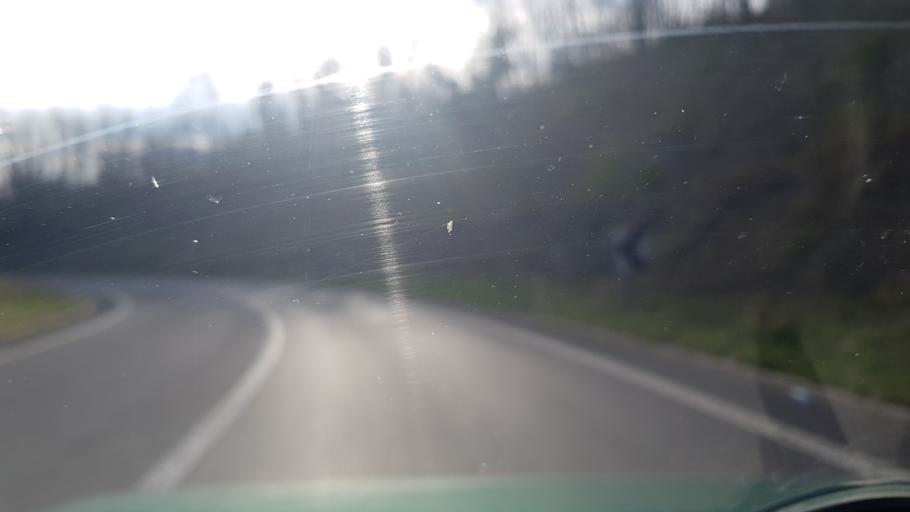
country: SI
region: Nova Gorica
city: Prvacina
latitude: 45.9192
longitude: 13.7106
